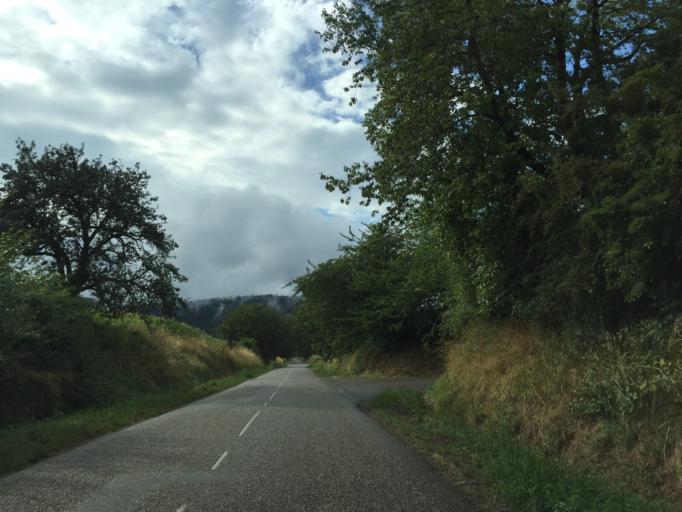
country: FR
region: Alsace
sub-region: Departement du Bas-Rhin
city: Soultz-sous-Forets
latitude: 48.9961
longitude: 7.8913
